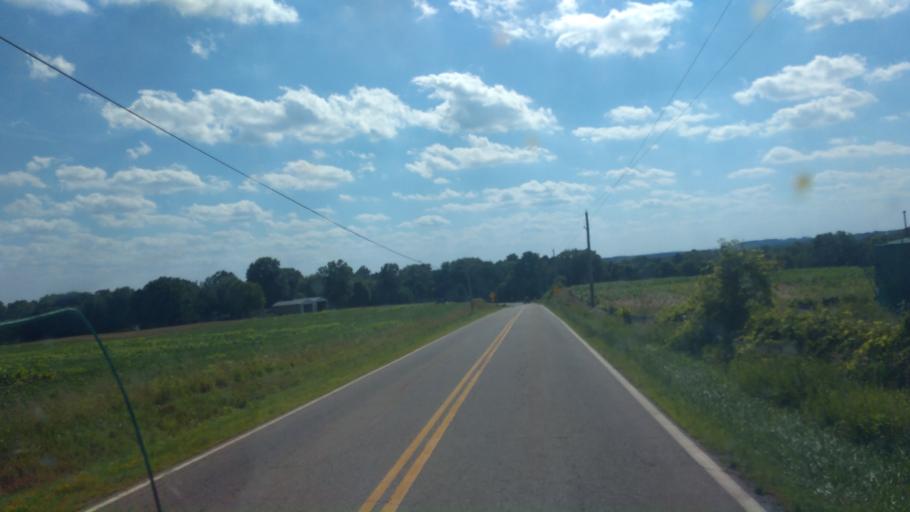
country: US
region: Ohio
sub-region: Stark County
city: Navarre
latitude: 40.7284
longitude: -81.5051
